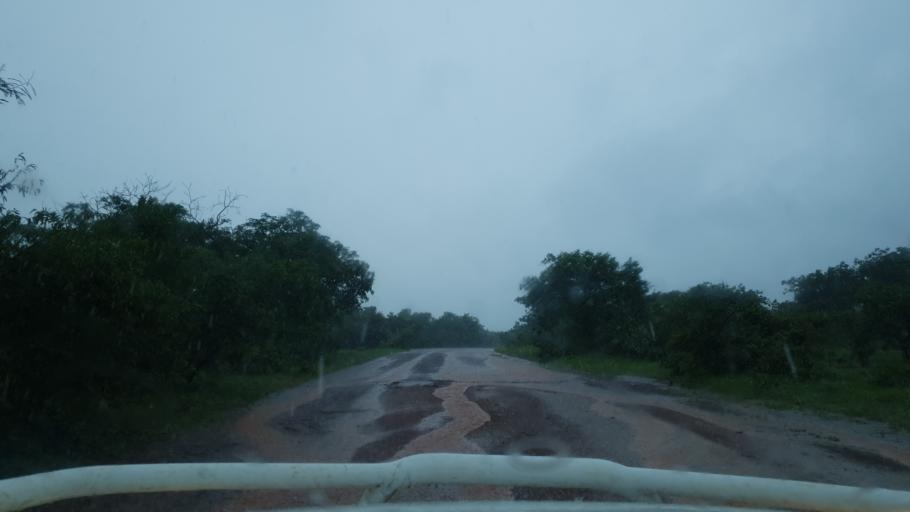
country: ML
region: Sikasso
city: Kolondieba
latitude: 11.6185
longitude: -6.6789
